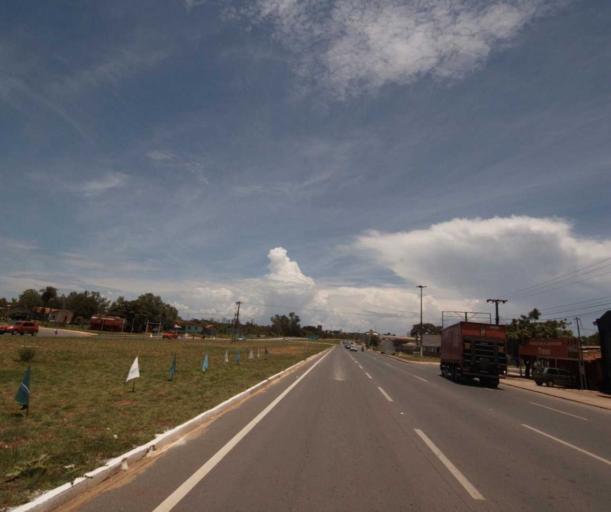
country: BR
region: Mato Grosso
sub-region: Varzea Grande
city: Varzea Grande
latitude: -15.6095
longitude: -56.1448
